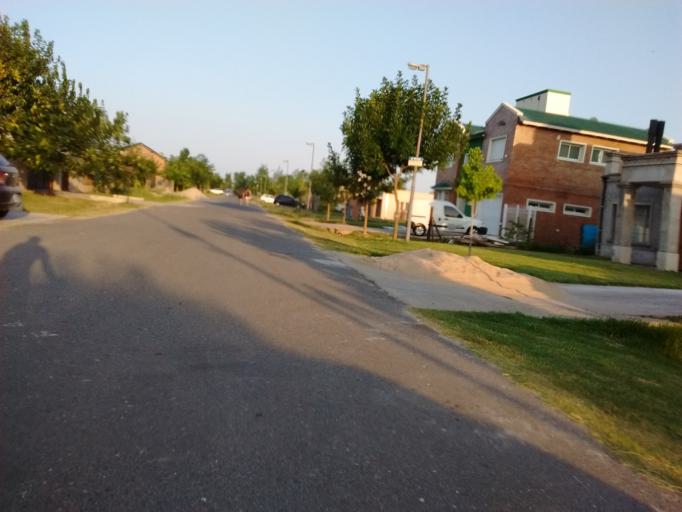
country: AR
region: Santa Fe
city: Funes
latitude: -32.9158
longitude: -60.7753
